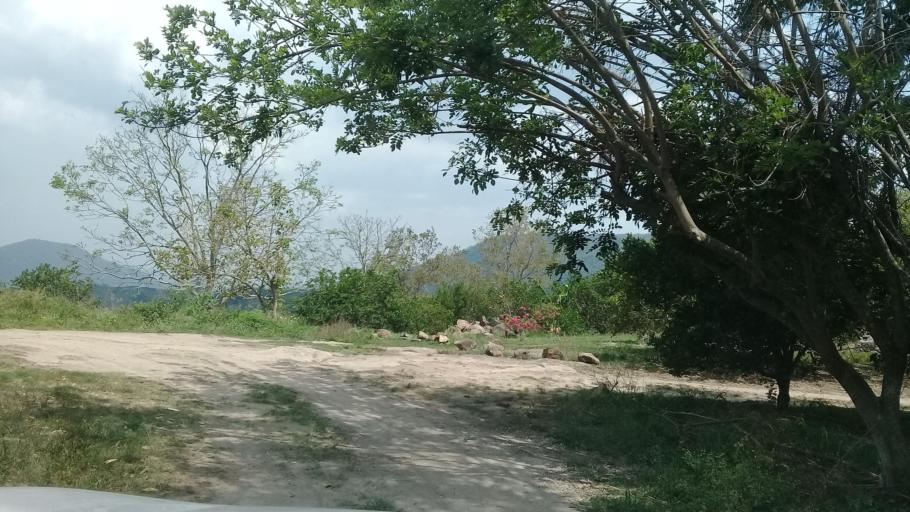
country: MX
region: Veracruz
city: Jalcomulco
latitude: 19.3832
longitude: -96.7933
